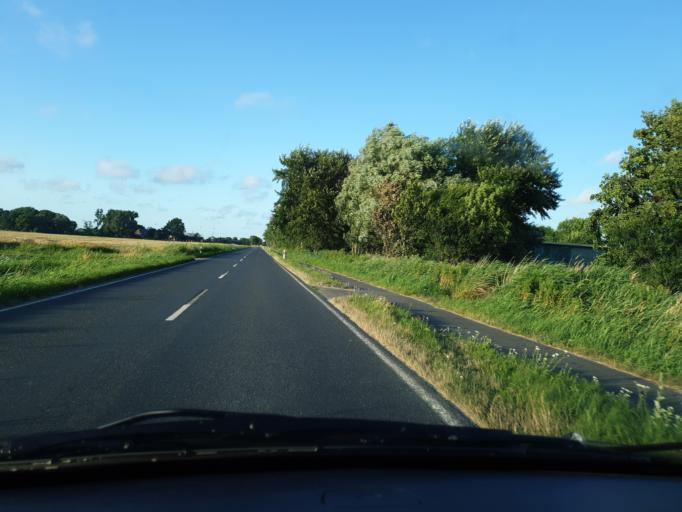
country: DE
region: Schleswig-Holstein
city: Wohrden
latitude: 54.1599
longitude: 8.9777
